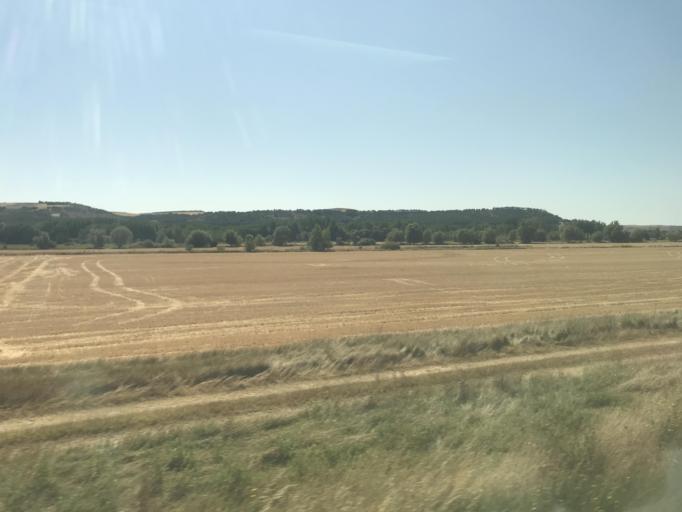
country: ES
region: Castille and Leon
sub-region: Provincia de Burgos
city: Pampliega
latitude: 42.2256
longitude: -3.9886
